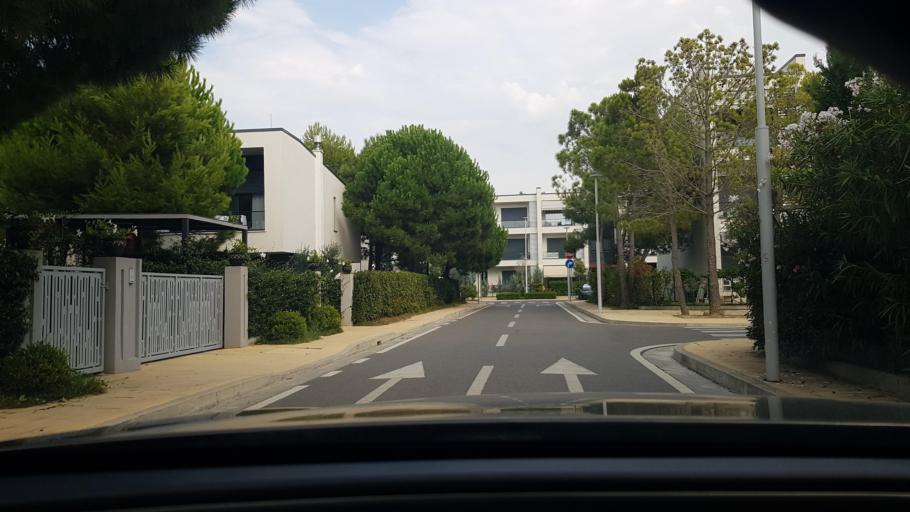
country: AL
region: Durres
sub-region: Rrethi i Durresit
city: Katundi i Ri
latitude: 41.4942
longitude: 19.5140
